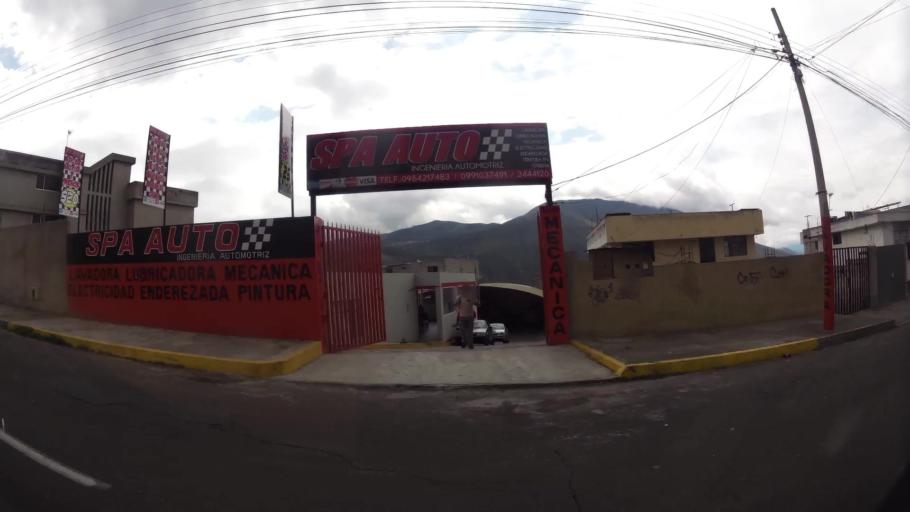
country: EC
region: Pichincha
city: Quito
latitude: -0.0842
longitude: -78.4715
